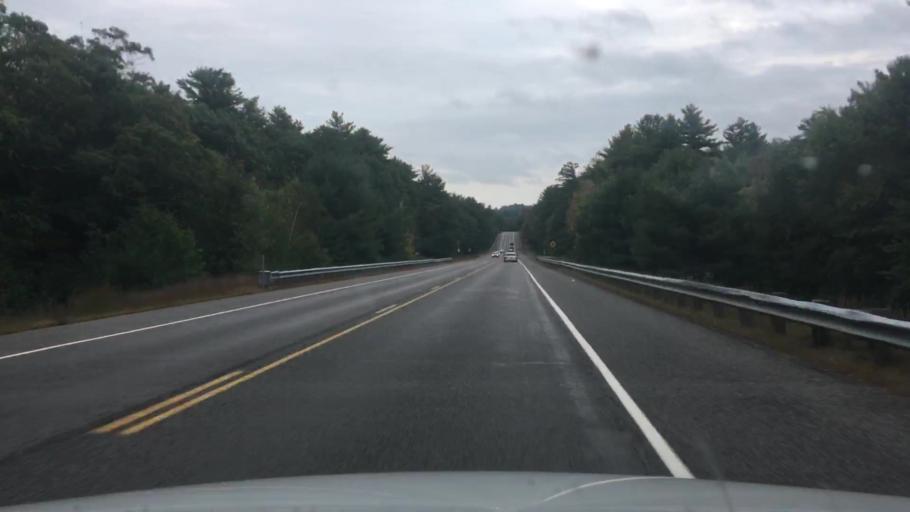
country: US
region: New Hampshire
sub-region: Carroll County
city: Wolfeboro
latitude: 43.4997
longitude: -71.2614
